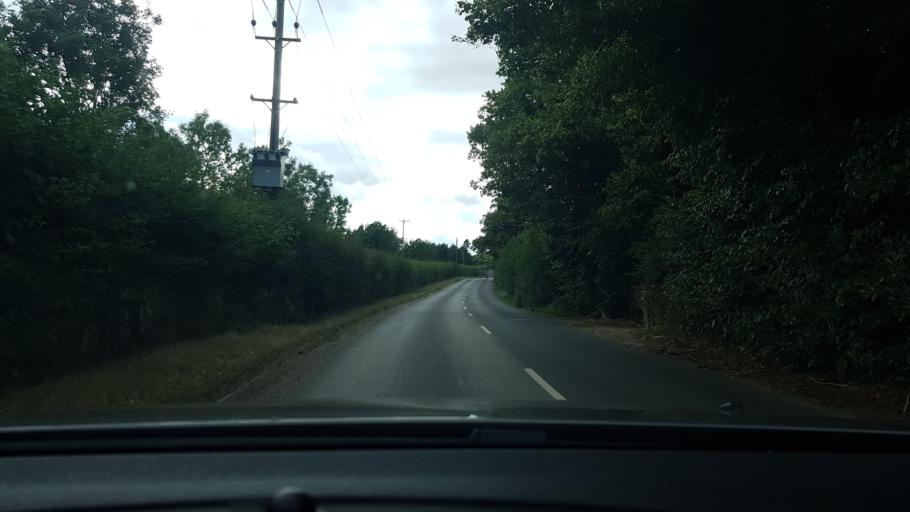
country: GB
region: England
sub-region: West Berkshire
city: Hermitage
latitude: 51.4580
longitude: -1.2983
